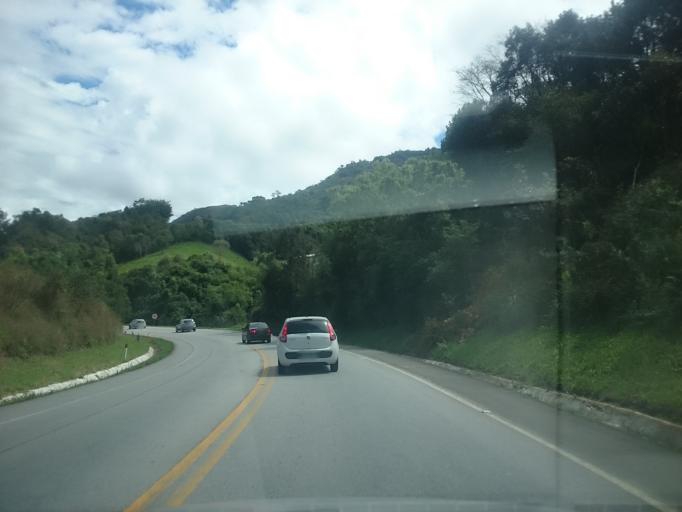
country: BR
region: Santa Catarina
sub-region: Anitapolis
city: Anitapolis
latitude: -27.6780
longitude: -49.2175
